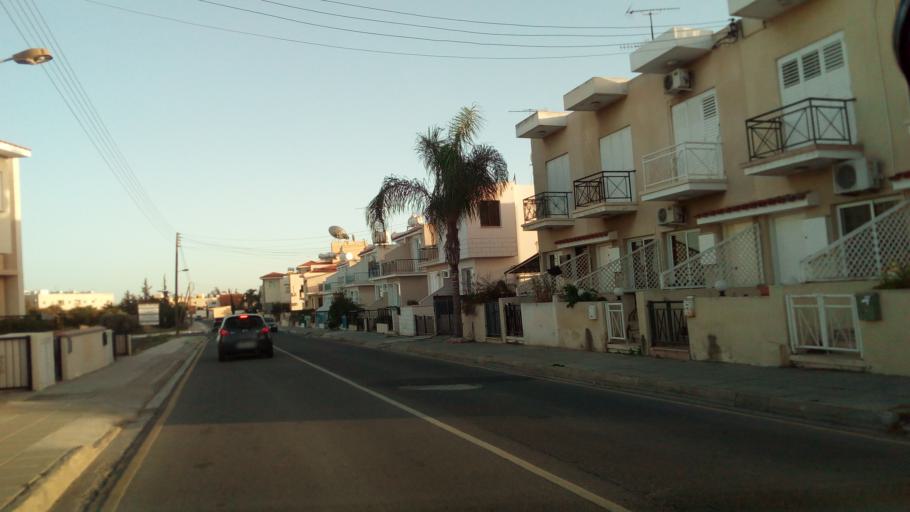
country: CY
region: Larnaka
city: Voroklini
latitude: 34.9790
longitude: 33.6612
